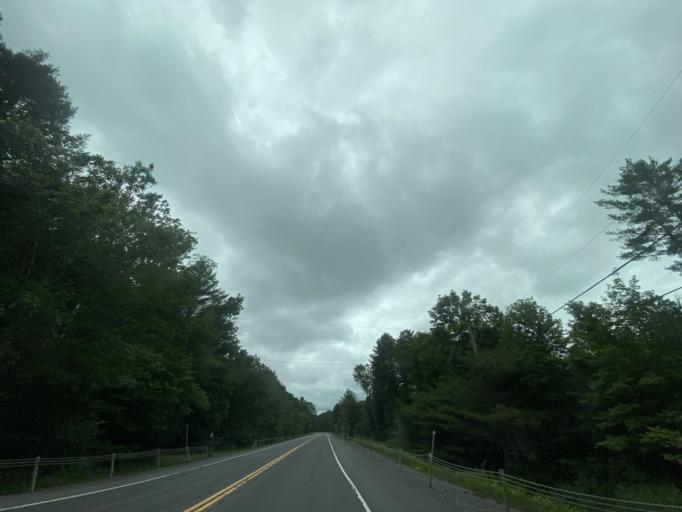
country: US
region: New York
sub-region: Greene County
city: Cairo
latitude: 42.3982
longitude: -73.9867
